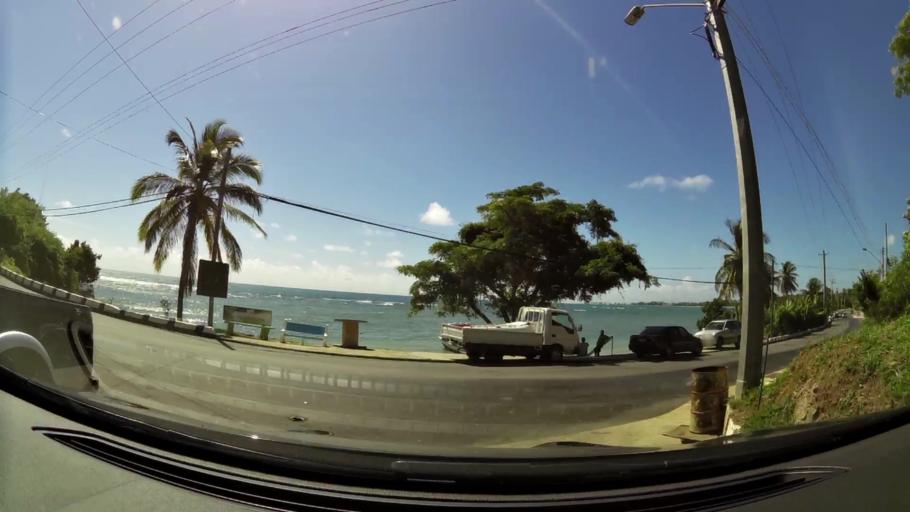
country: TT
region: Tobago
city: Scarborough
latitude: 11.1667
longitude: -60.7617
